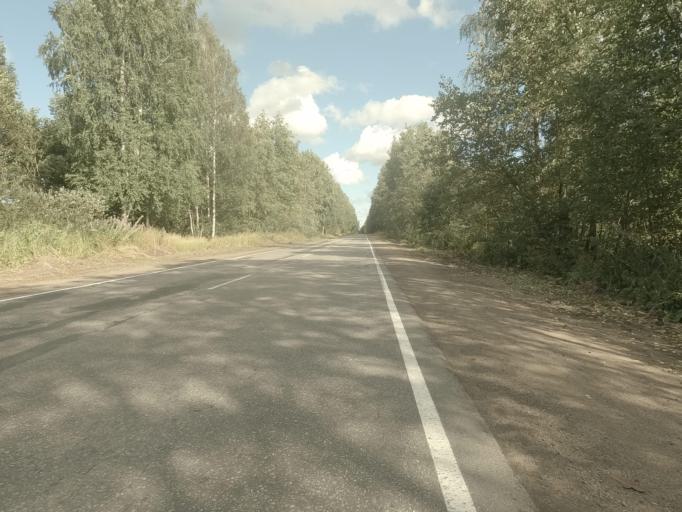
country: RU
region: Leningrad
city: Romanovka
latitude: 60.0228
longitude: 30.7133
